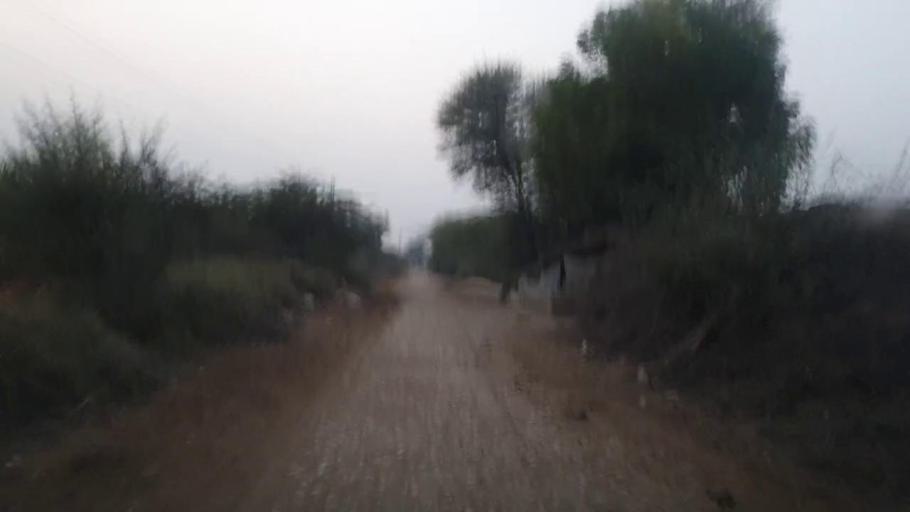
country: PK
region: Sindh
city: Karaundi
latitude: 26.9302
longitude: 68.4381
